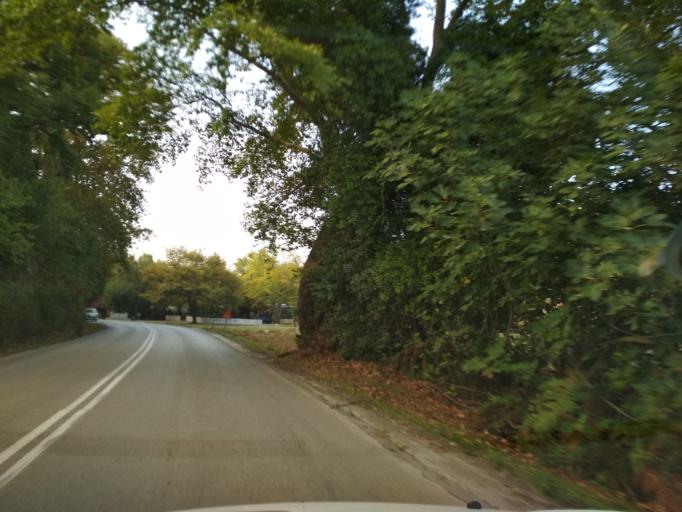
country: GR
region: Central Greece
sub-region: Nomos Evvoias
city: Mantoudi
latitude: 38.7687
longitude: 23.4761
